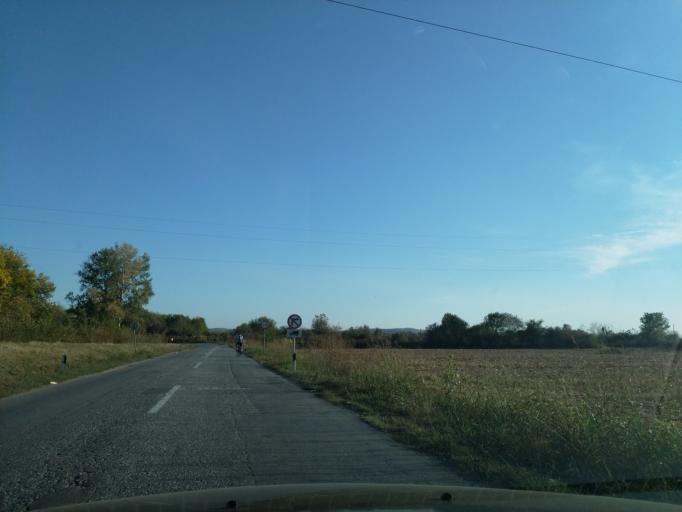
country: RS
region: Central Serbia
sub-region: Pomoravski Okrug
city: Svilajnac
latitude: 44.2246
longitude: 21.1482
